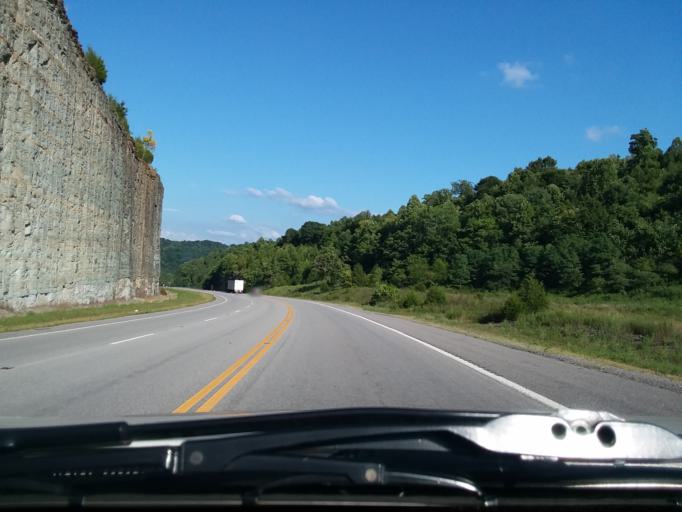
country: US
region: Tennessee
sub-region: Clay County
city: Celina
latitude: 36.5816
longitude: -85.5600
